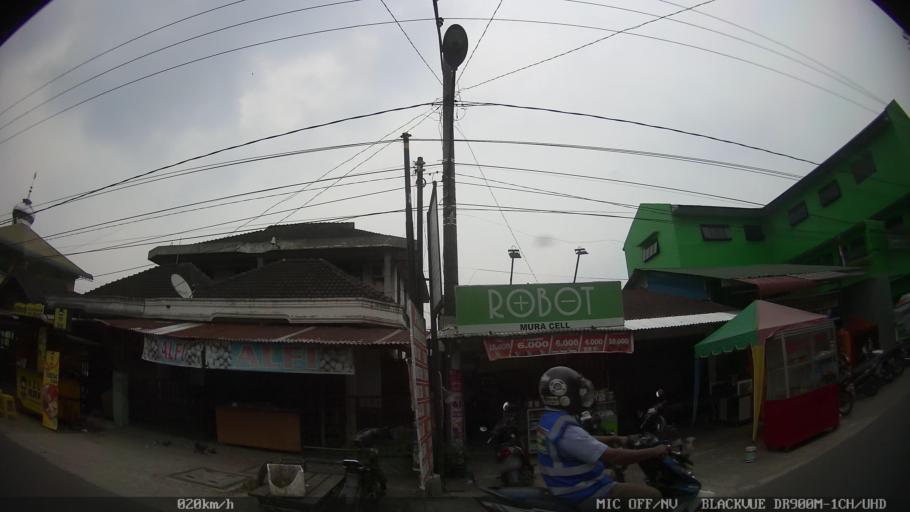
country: ID
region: North Sumatra
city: Deli Tua
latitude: 3.5524
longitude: 98.7096
